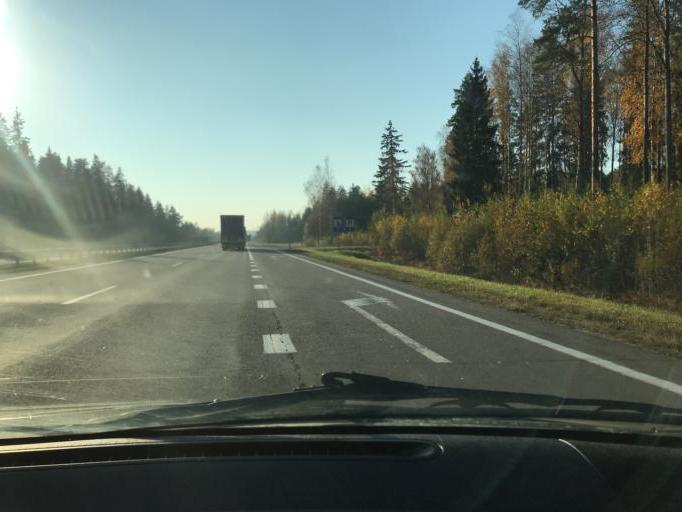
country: BY
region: Minsk
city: Krupki
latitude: 54.3054
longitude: 28.9907
